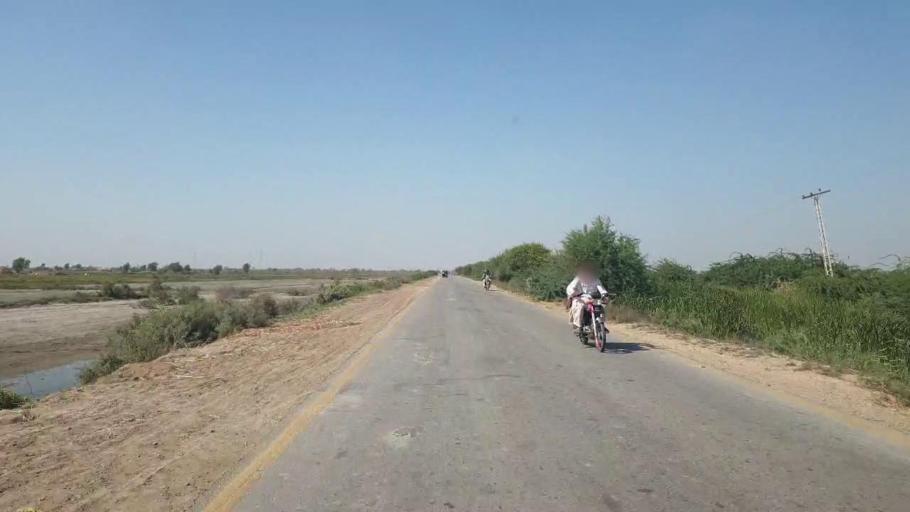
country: PK
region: Sindh
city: Rajo Khanani
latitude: 25.0496
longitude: 68.8087
